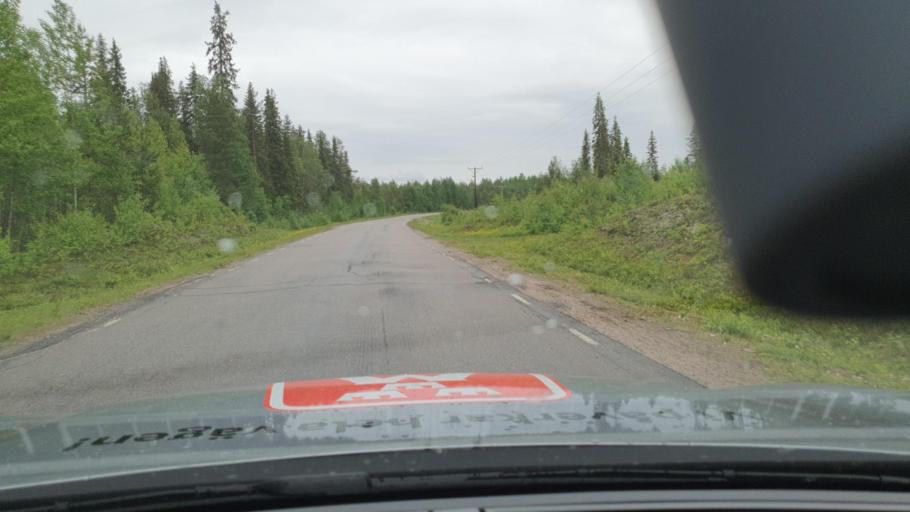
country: SE
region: Norrbotten
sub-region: Pajala Kommun
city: Pajala
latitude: 66.7476
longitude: 23.1679
